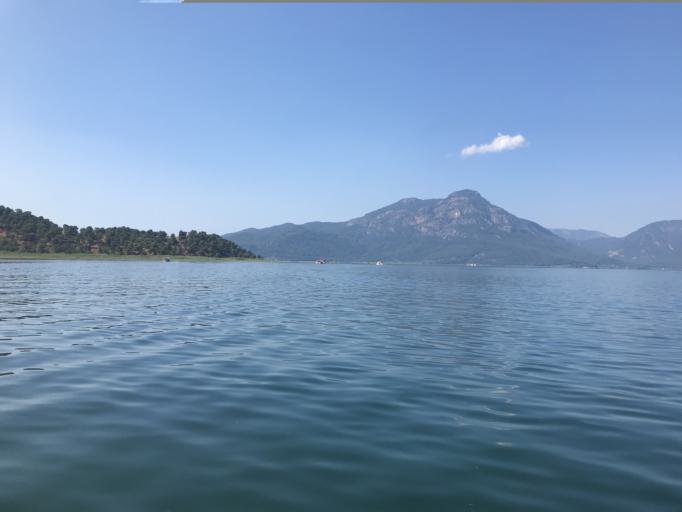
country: TR
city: Dalyan
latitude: 36.9041
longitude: 28.6477
